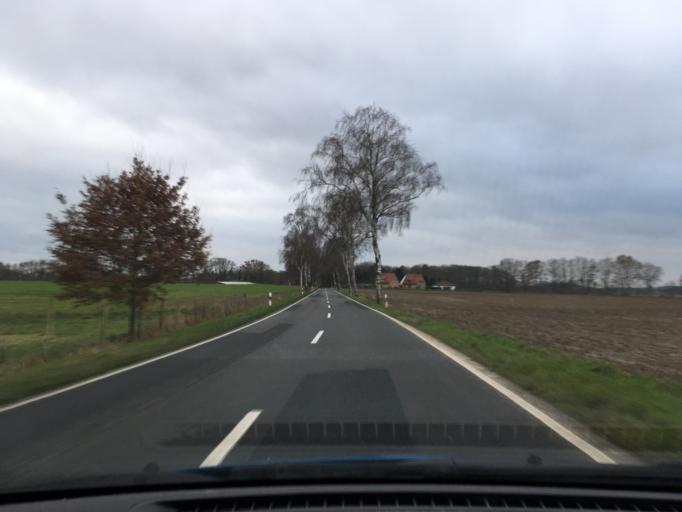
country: DE
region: Lower Saxony
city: Ebstorf
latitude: 53.0073
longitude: 10.4166
